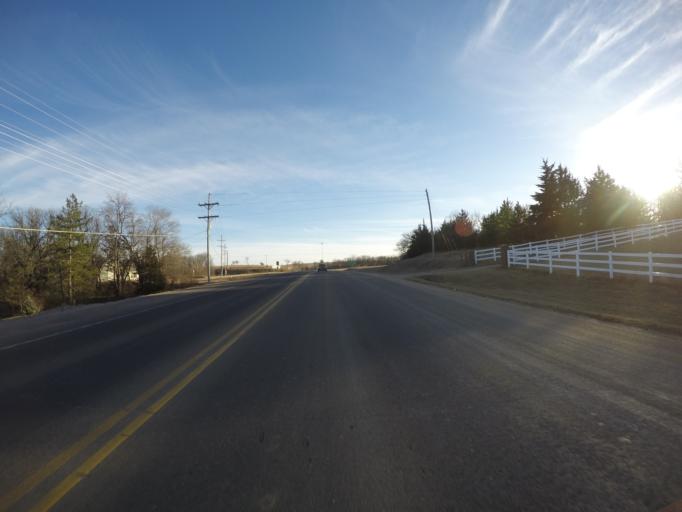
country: US
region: Kansas
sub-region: Marshall County
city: Marysville
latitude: 39.8440
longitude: -96.6668
